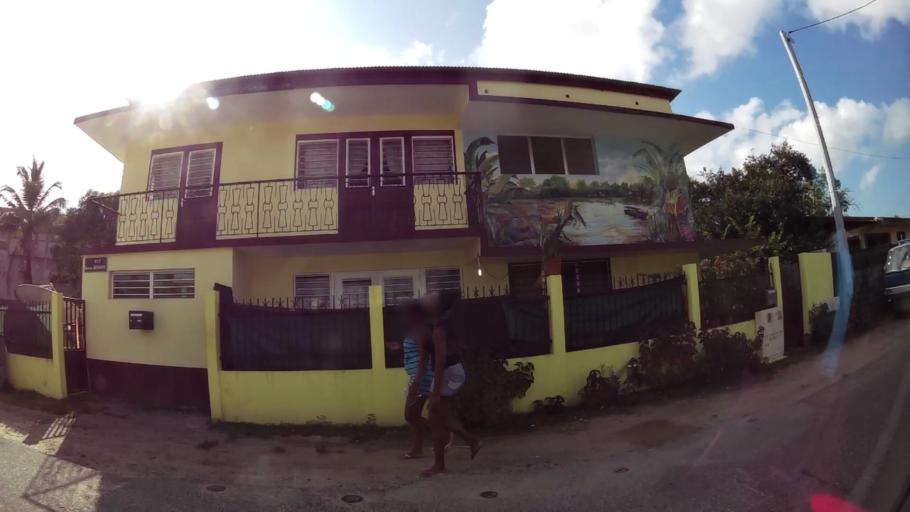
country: GF
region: Guyane
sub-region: Guyane
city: Cayenne
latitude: 4.9328
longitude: -52.3197
